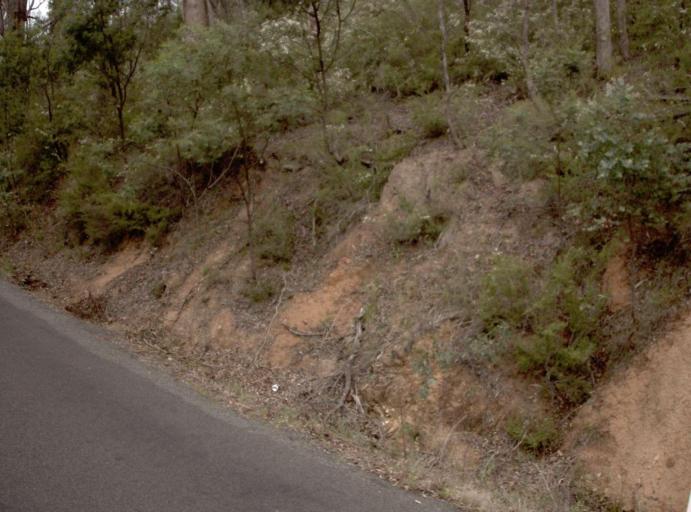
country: AU
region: Victoria
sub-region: East Gippsland
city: Bairnsdale
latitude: -37.4745
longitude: 147.2147
